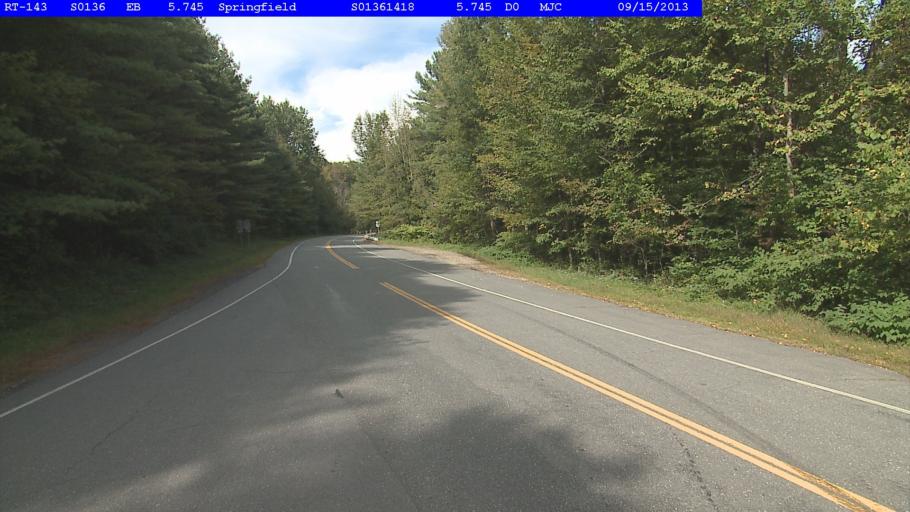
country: US
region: Vermont
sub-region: Windsor County
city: Springfield
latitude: 43.3314
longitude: -72.4122
